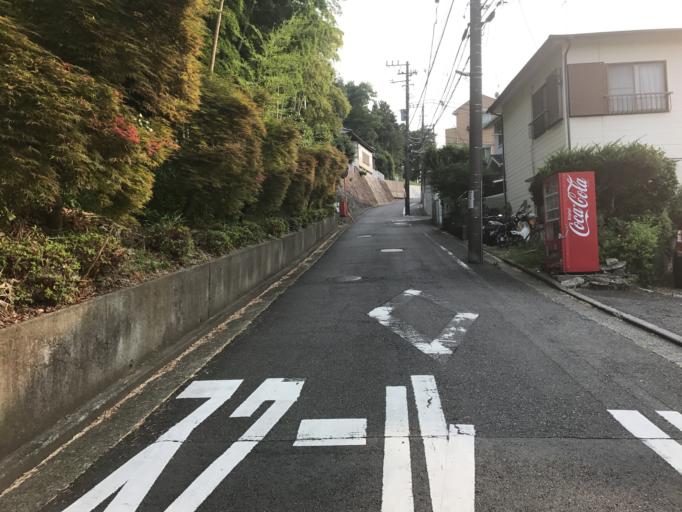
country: JP
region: Kanagawa
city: Yokohama
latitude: 35.5450
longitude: 139.5882
